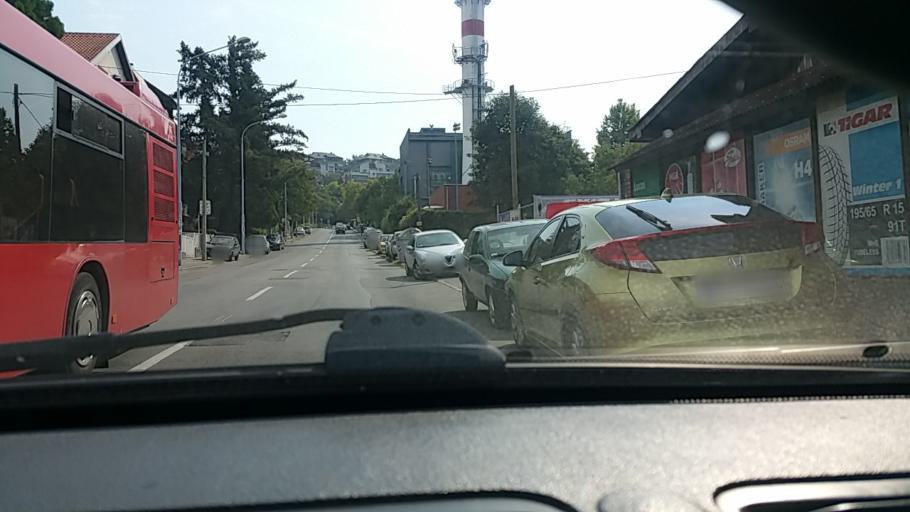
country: RS
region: Central Serbia
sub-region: Belgrade
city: Rakovica
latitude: 44.7501
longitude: 20.4535
